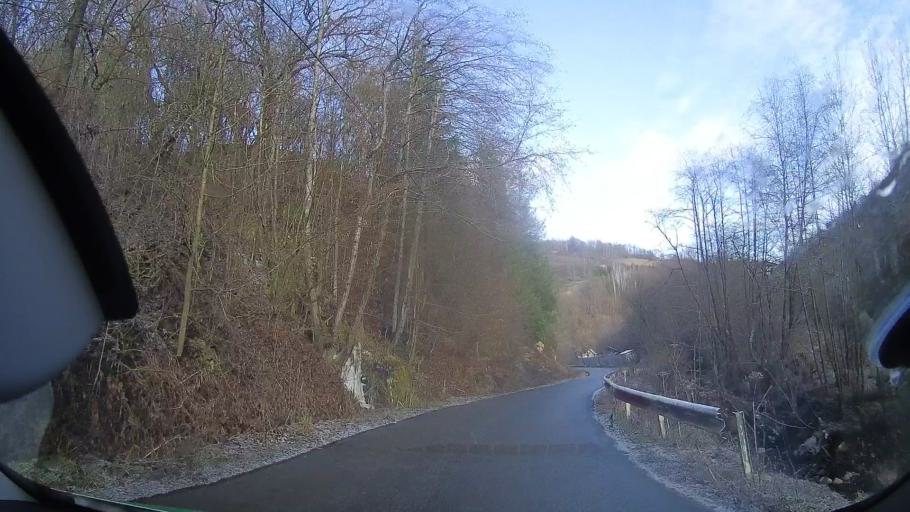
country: RO
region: Alba
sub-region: Comuna Sohodol
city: Sohodol
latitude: 46.3471
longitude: 23.0201
